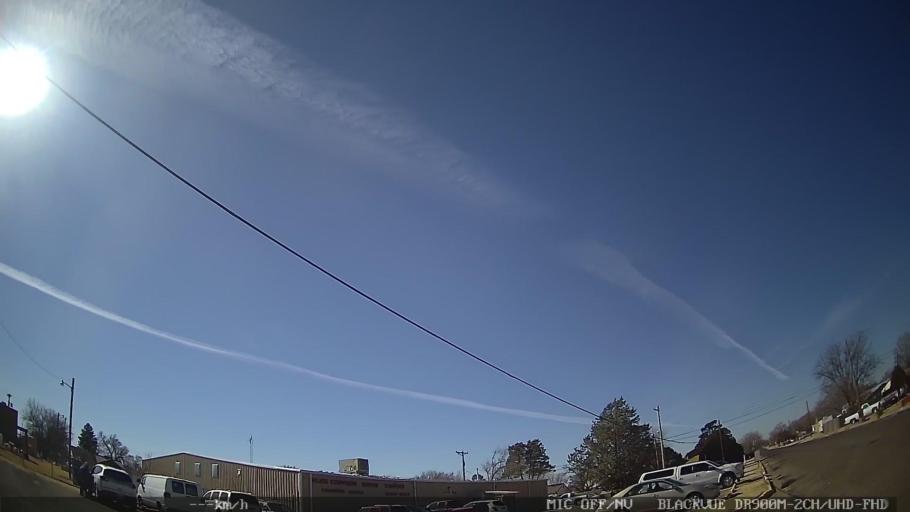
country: US
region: New Mexico
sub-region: Curry County
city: Clovis
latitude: 34.4128
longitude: -103.2190
